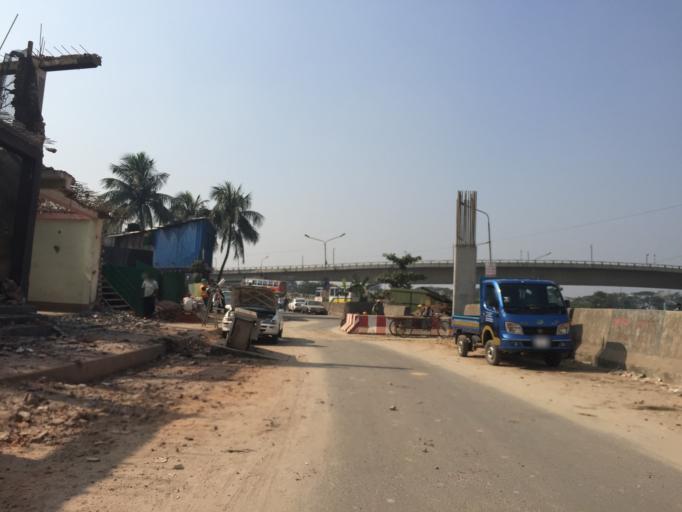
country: BD
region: Dhaka
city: Tungi
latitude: 23.8248
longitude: 90.4226
